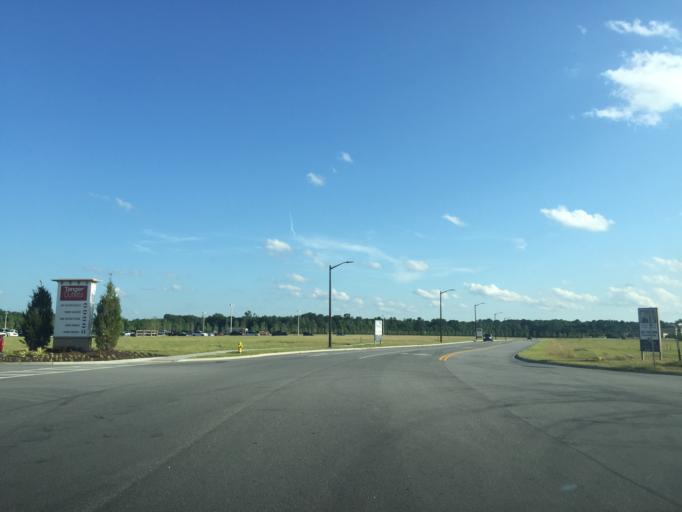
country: US
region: Georgia
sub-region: Chatham County
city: Pooler
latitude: 32.1353
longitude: -81.2460
